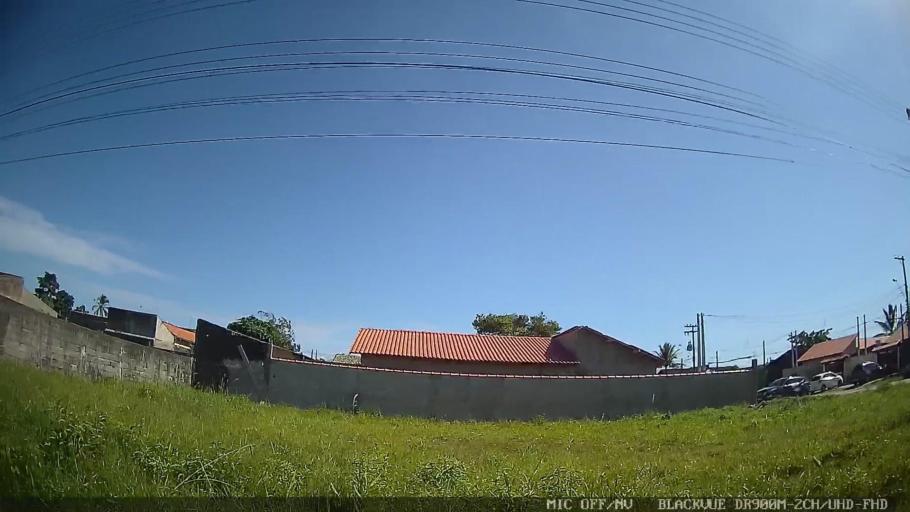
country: BR
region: Sao Paulo
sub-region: Itanhaem
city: Itanhaem
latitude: -24.2135
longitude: -46.8597
